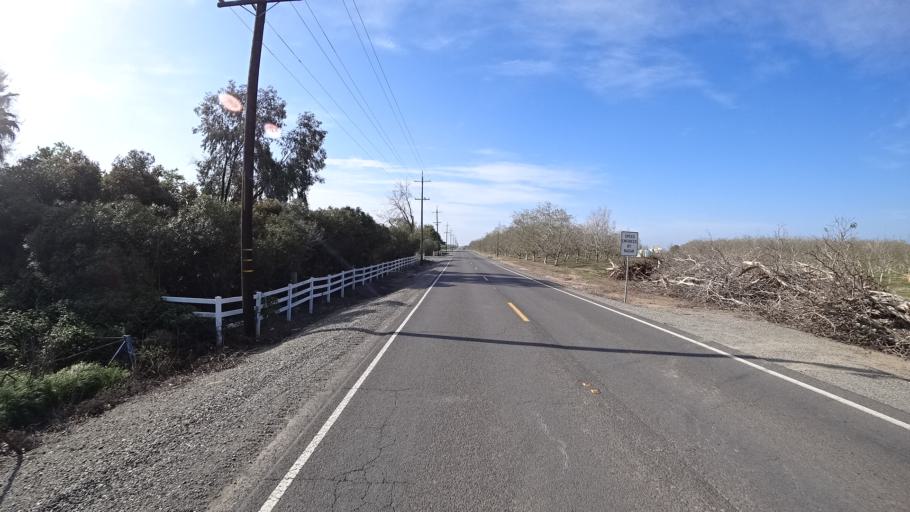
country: US
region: California
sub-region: Glenn County
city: Hamilton City
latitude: 39.6270
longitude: -122.0070
